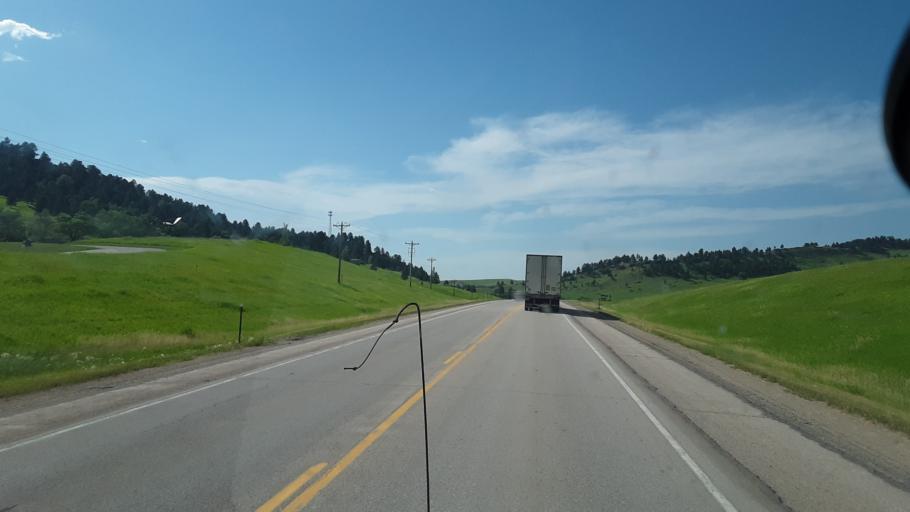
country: US
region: South Dakota
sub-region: Lawrence County
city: Deadwood
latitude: 44.4779
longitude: -103.6393
